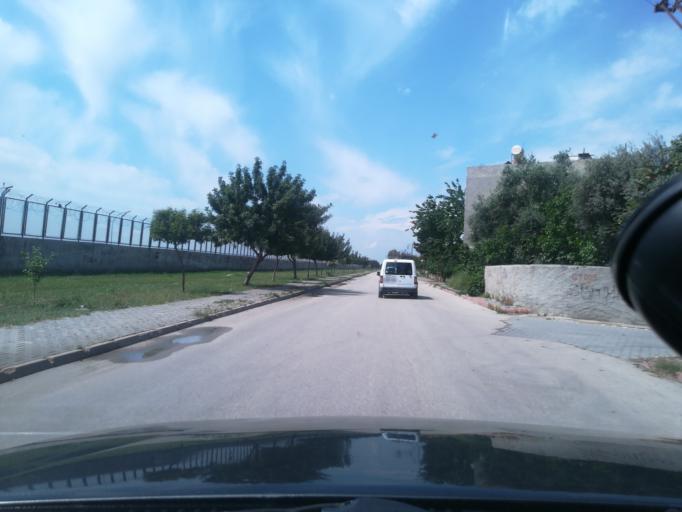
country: TR
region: Adana
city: Seyhan
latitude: 36.9861
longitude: 35.2840
